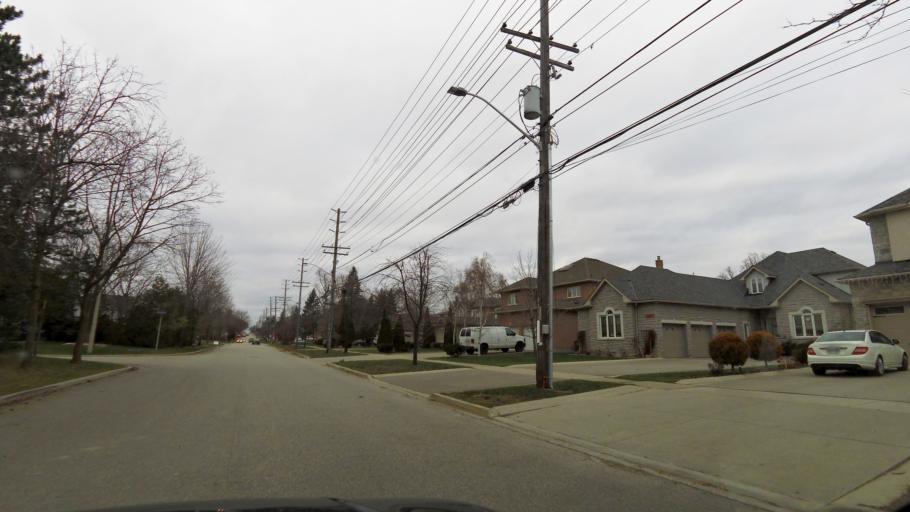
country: CA
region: Ontario
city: Mississauga
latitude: 43.5530
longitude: -79.6367
